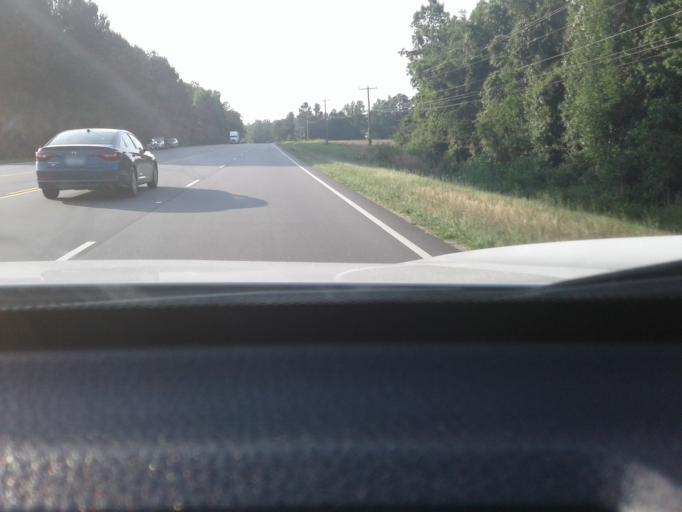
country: US
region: North Carolina
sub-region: Harnett County
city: Buies Creek
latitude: 35.3941
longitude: -78.7300
